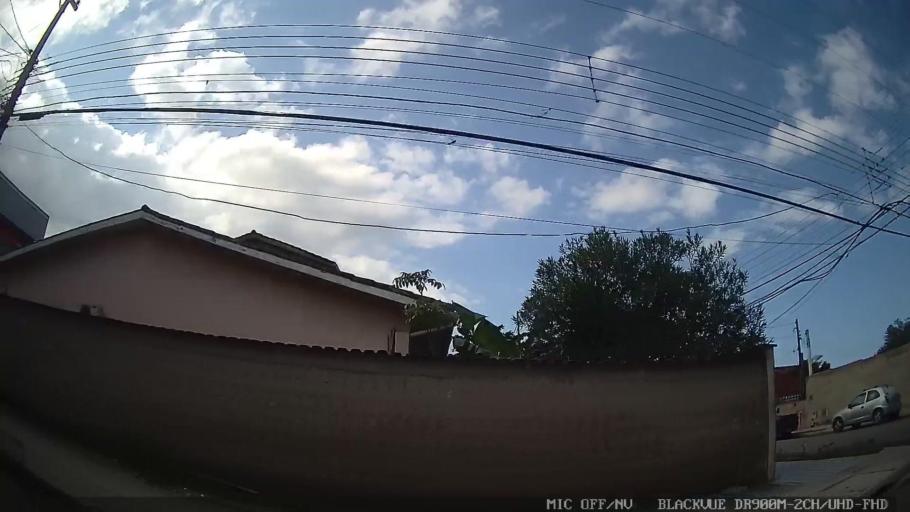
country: BR
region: Sao Paulo
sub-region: Guaruja
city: Guaruja
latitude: -23.9959
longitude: -46.2798
